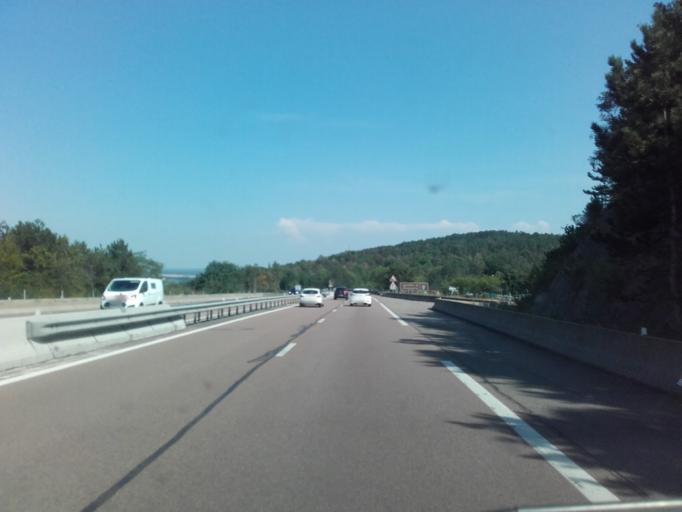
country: FR
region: Bourgogne
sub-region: Departement de la Cote-d'Or
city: Savigny-les-Beaune
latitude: 47.0585
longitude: 4.8120
